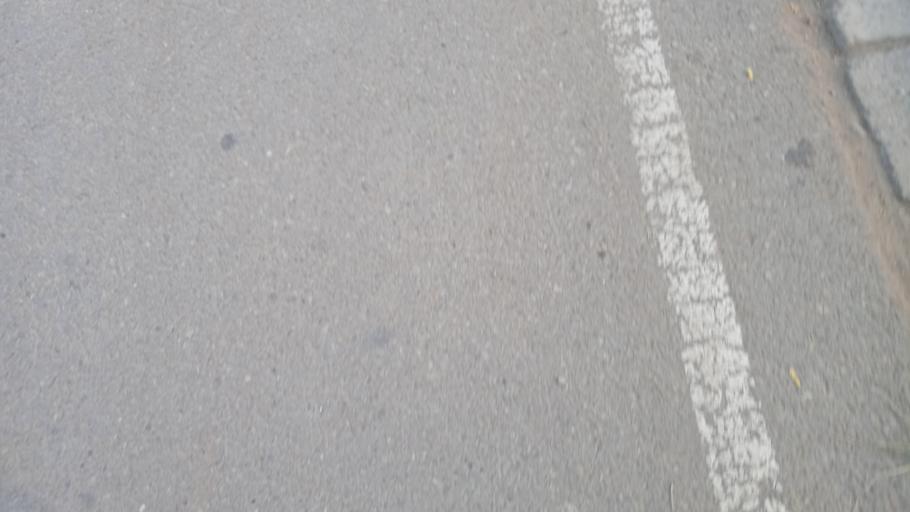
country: IN
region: Chandigarh
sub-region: Chandigarh
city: Chandigarh
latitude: 30.7435
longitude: 76.7456
